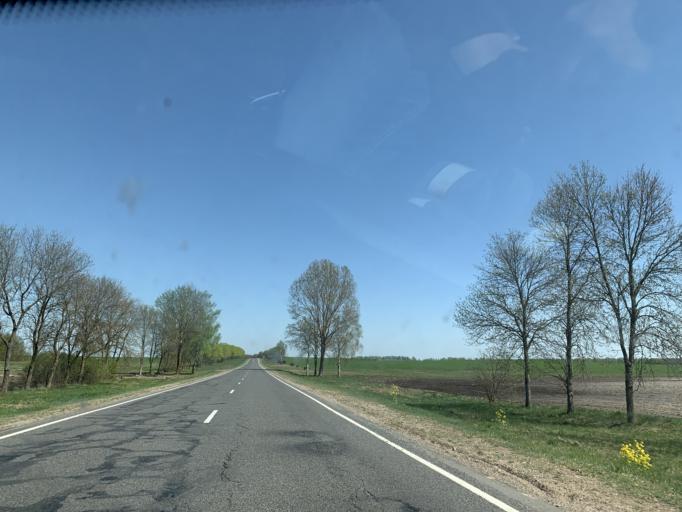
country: BY
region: Minsk
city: Tsimkavichy
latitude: 53.2475
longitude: 26.8849
